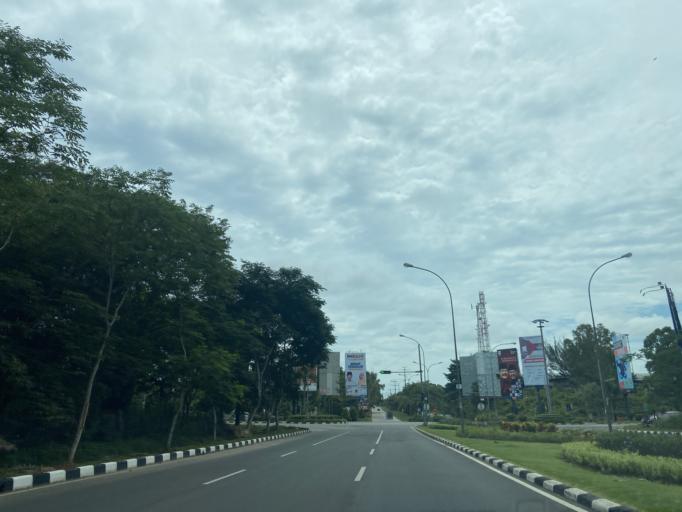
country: SG
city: Singapore
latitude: 1.1273
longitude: 104.1078
